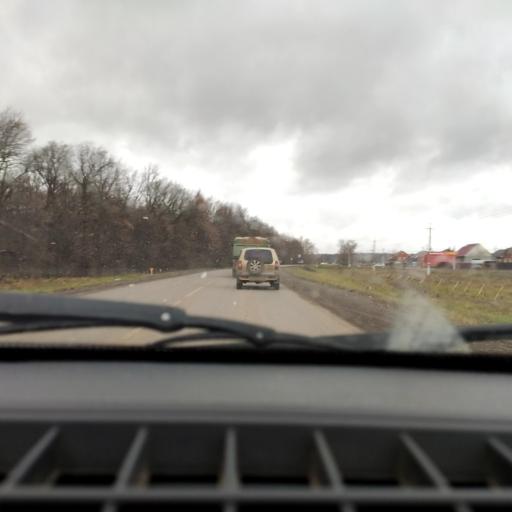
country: RU
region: Bashkortostan
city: Mikhaylovka
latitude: 54.8225
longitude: 55.8829
